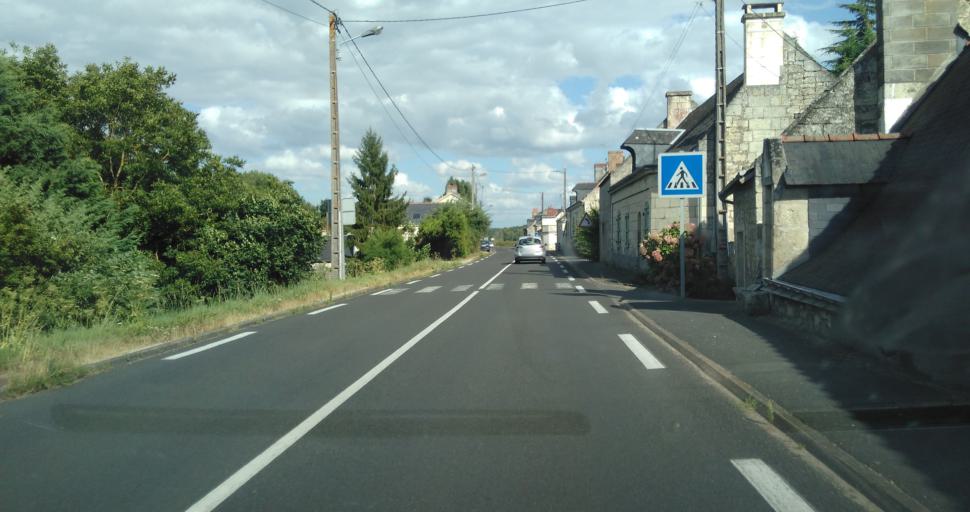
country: FR
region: Centre
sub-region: Departement d'Indre-et-Loire
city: La Chapelle-sur-Loire
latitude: 47.2394
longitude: 0.1883
